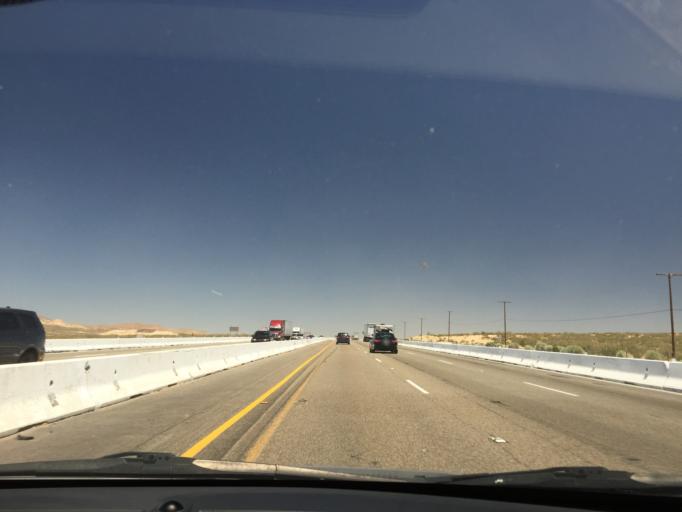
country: US
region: California
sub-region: San Bernardino County
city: Victorville
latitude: 34.5642
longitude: -117.2834
